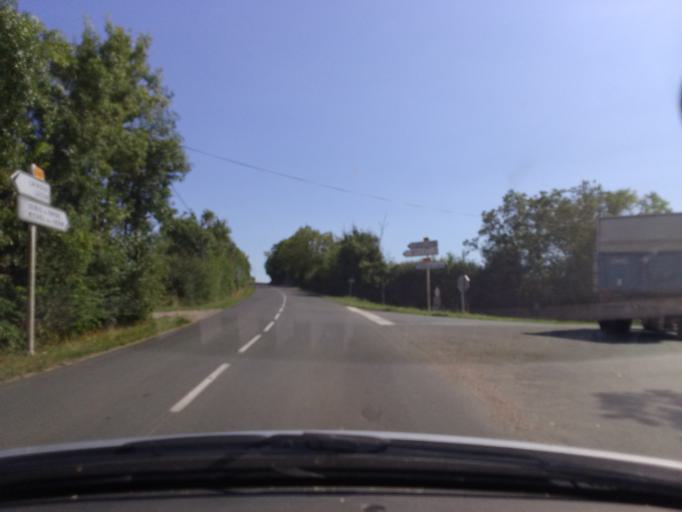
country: FR
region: Pays de la Loire
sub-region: Departement de la Vendee
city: Les Magnils-Reigniers
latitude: 46.4410
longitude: -1.2648
